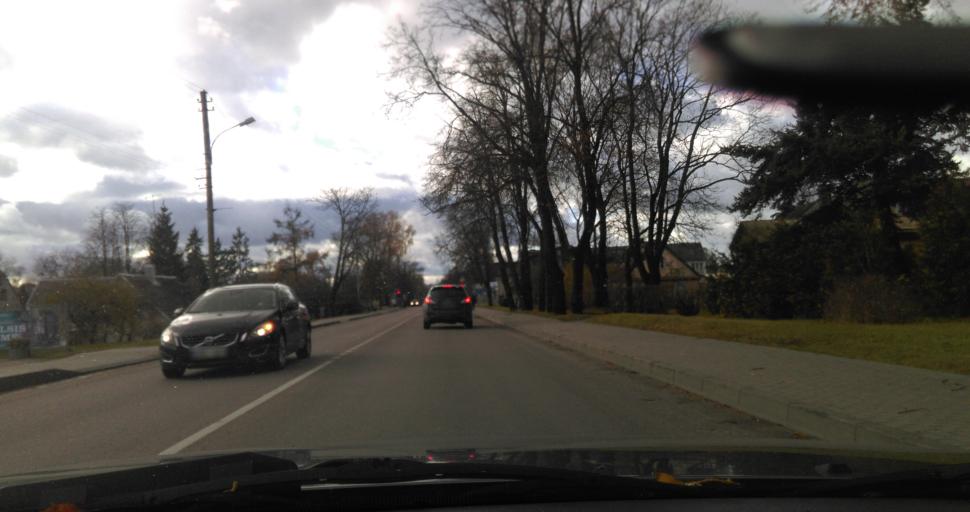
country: LT
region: Utenos apskritis
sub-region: Utena
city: Utena
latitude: 55.5005
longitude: 25.6117
